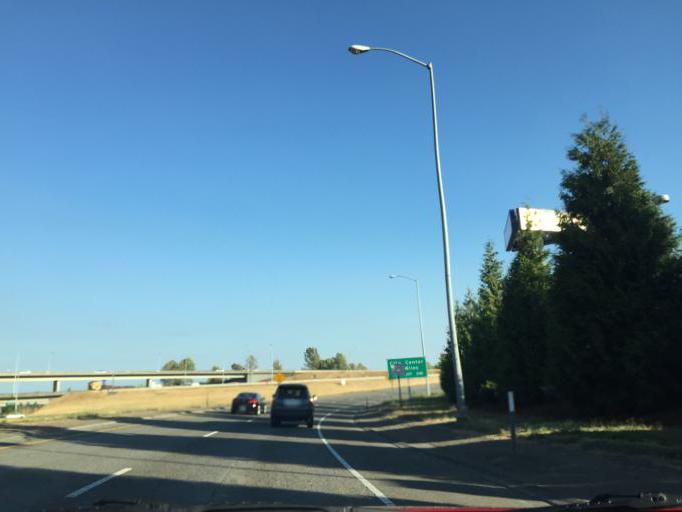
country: US
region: Washington
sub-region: Clark County
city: Mill Plain
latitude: 45.5723
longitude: -122.5527
